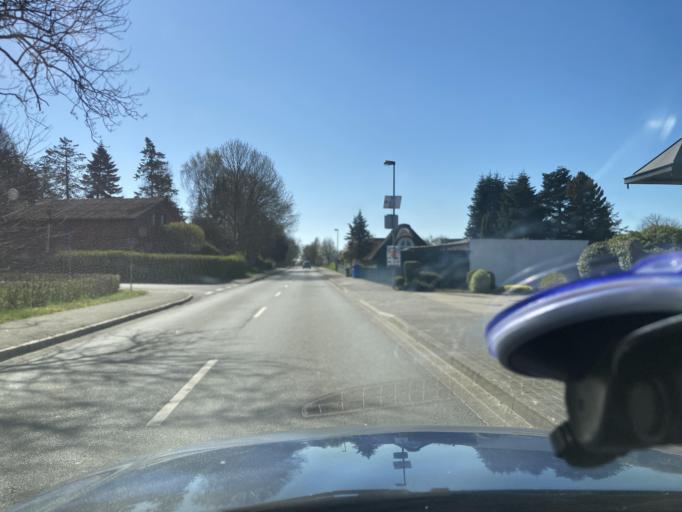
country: DE
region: Schleswig-Holstein
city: Sarzbuttel
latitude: 54.1147
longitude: 9.1856
